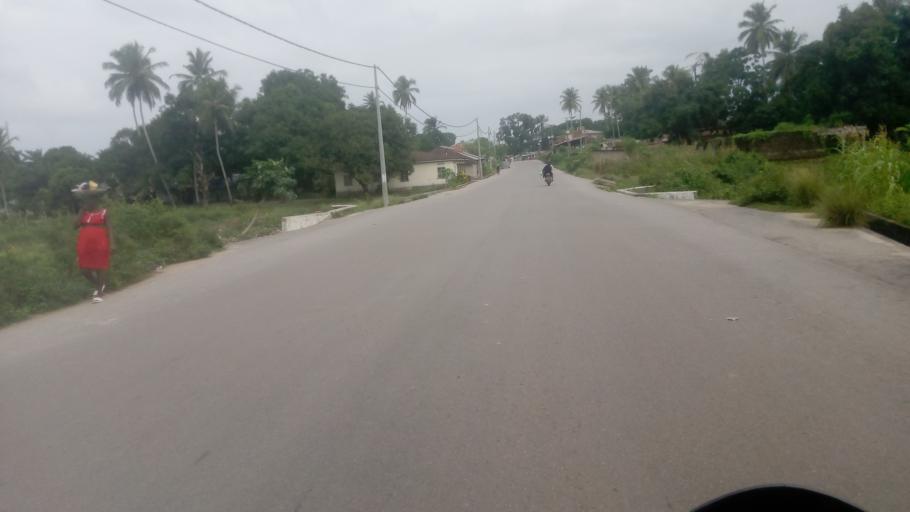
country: SL
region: Northern Province
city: Lunsar
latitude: 8.6883
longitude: -12.5358
